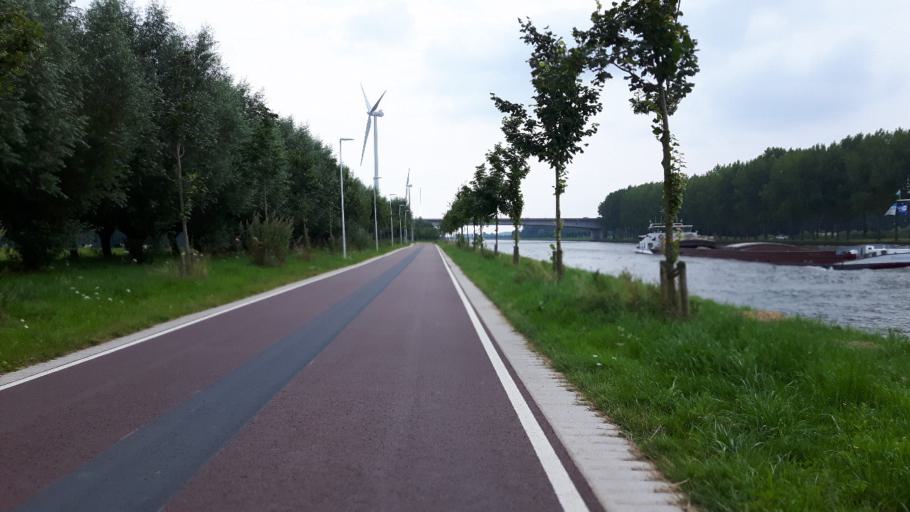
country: NL
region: Utrecht
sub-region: Gemeente Utrecht
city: Lunetten
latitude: 52.0283
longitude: 5.1264
